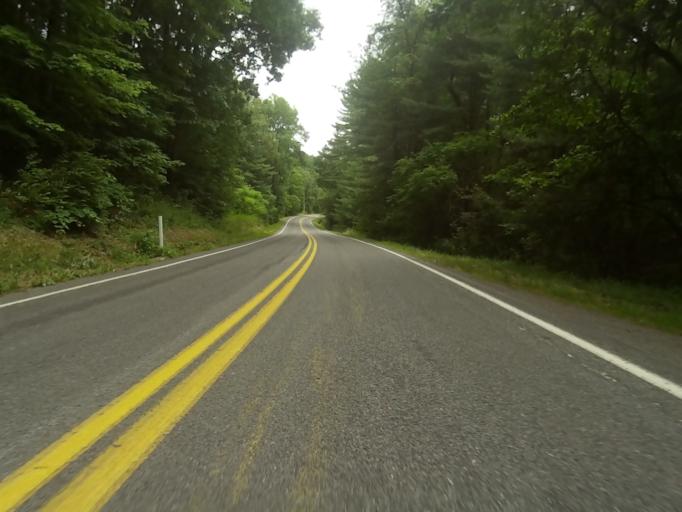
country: US
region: Pennsylvania
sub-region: Centre County
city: Stormstown
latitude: 40.7321
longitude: -77.9766
